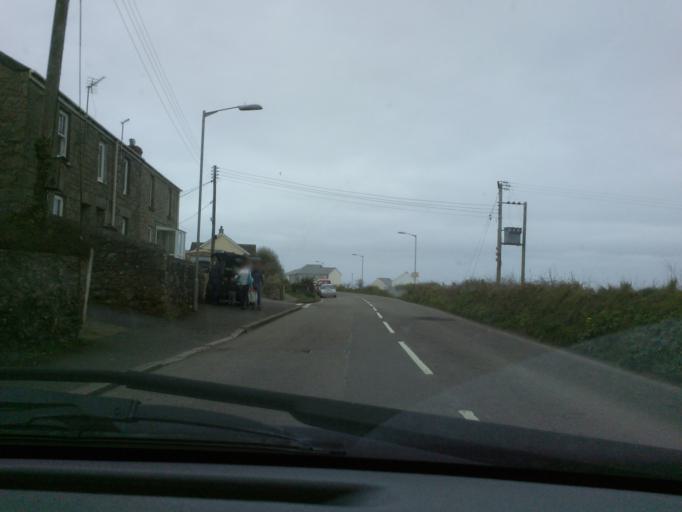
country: GB
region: England
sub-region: Cornwall
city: Saint Just
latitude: 50.1212
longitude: -5.6755
